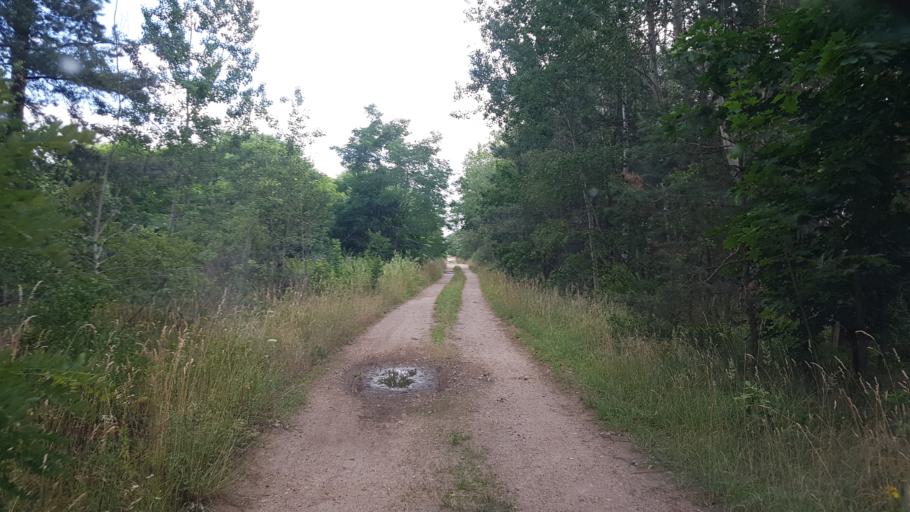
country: DE
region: Brandenburg
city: Finsterwalde
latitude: 51.6561
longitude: 13.6962
